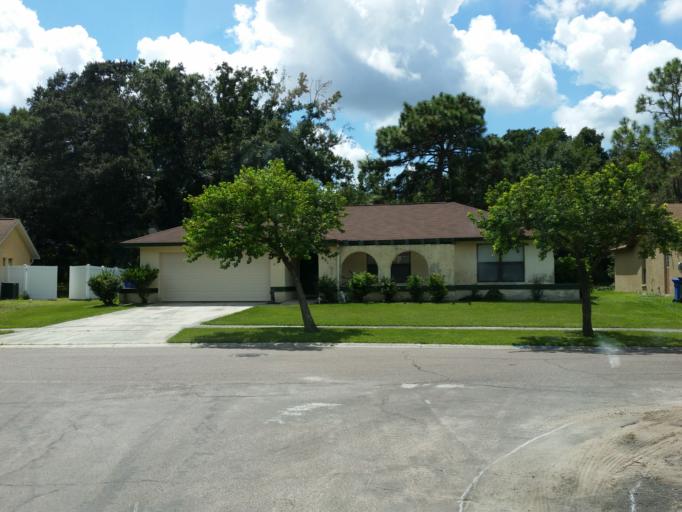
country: US
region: Florida
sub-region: Hillsborough County
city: Bloomingdale
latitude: 27.8761
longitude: -82.2712
